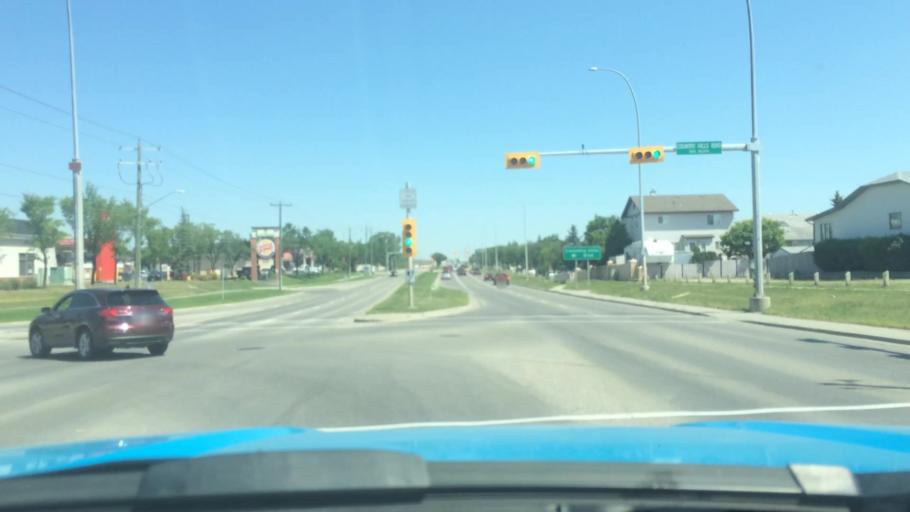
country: CA
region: Alberta
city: Calgary
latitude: 51.1542
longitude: -114.0563
